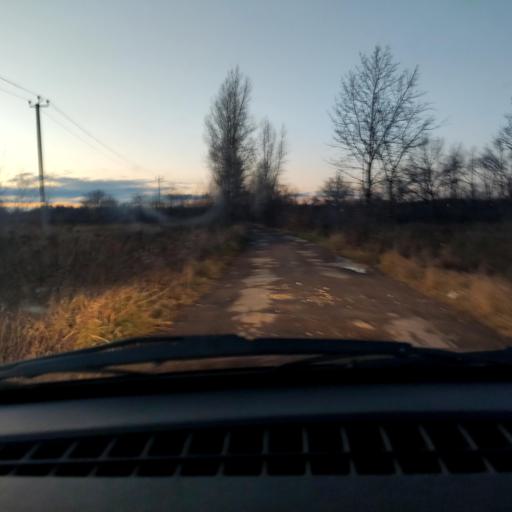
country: RU
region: Bashkortostan
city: Ufa
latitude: 54.6527
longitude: 55.8910
